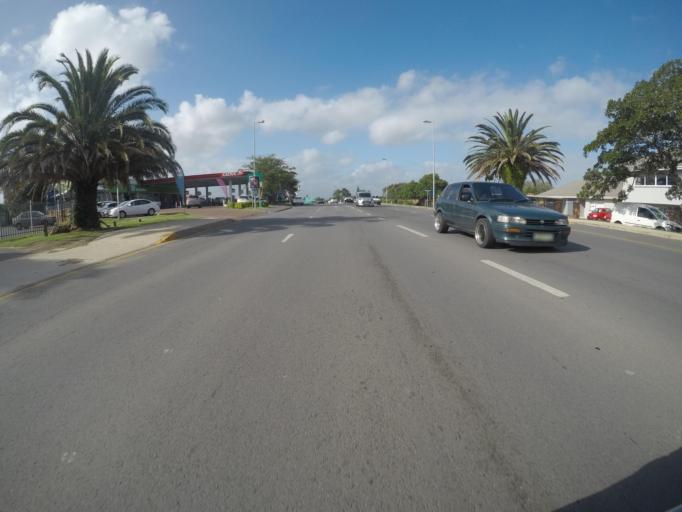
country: ZA
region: Eastern Cape
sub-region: Buffalo City Metropolitan Municipality
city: East London
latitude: -32.9613
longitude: 27.9348
